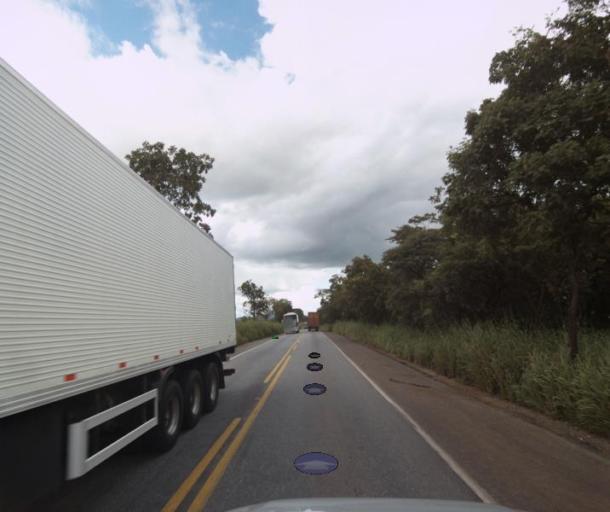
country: BR
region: Goias
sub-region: Porangatu
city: Porangatu
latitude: -13.2923
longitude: -49.1242
